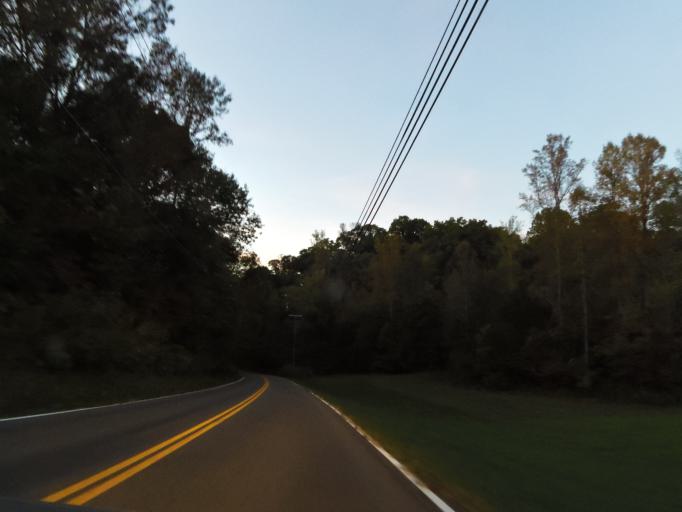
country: US
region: Tennessee
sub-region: Knox County
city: Mascot
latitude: 36.0034
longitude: -83.6371
